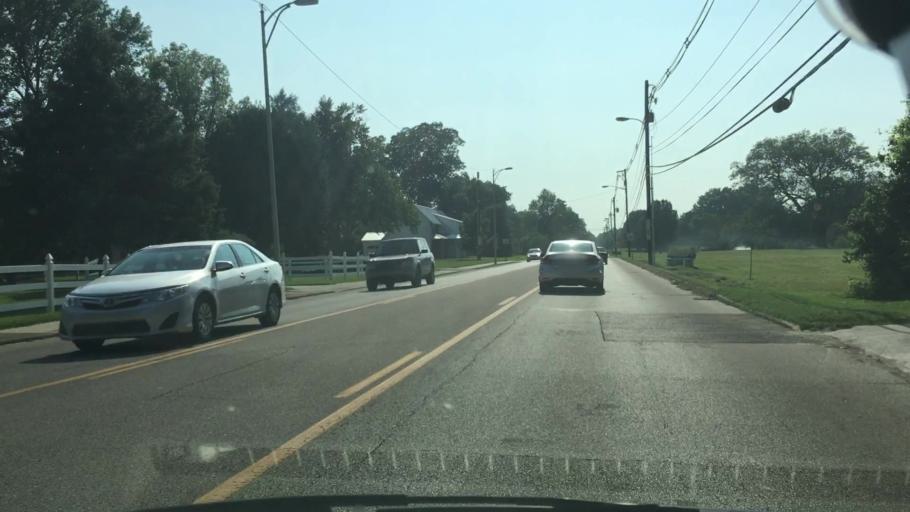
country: US
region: Indiana
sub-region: Vanderburgh County
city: Evansville
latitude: 37.9697
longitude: -87.4997
